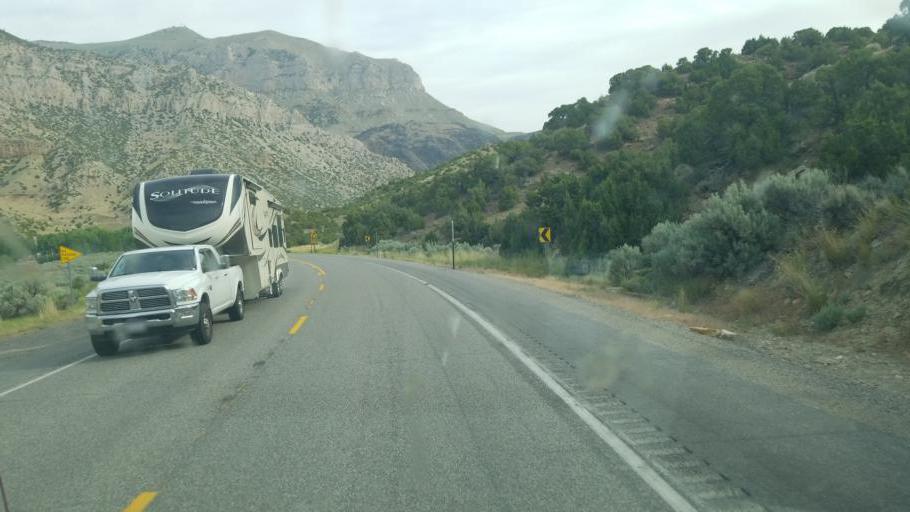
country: US
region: Wyoming
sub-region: Hot Springs County
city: Thermopolis
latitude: 43.4270
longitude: -108.1759
